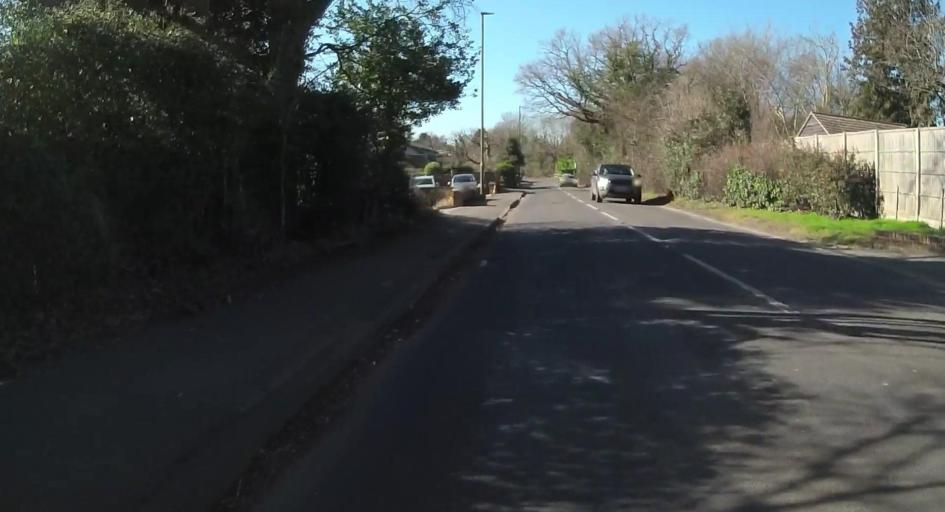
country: GB
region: England
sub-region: Surrey
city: Ottershaw
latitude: 51.3657
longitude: -0.5217
